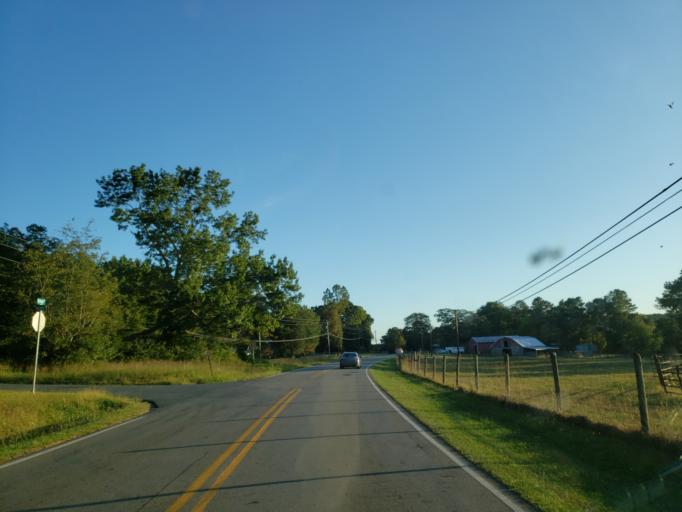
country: US
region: Georgia
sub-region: Pickens County
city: Jasper
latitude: 34.4418
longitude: -84.4212
